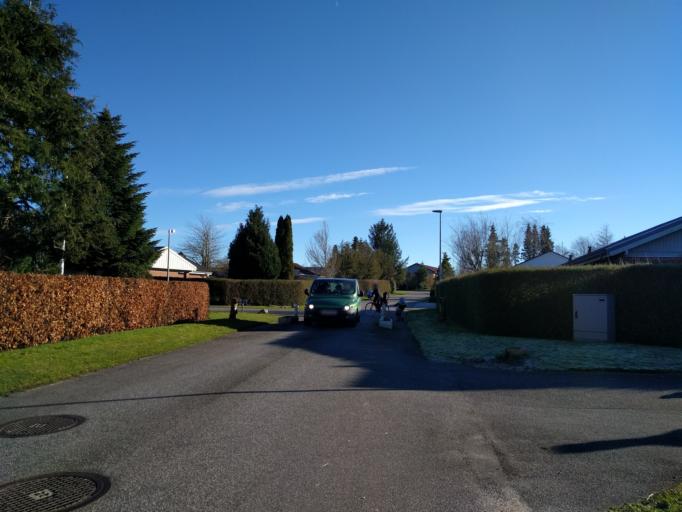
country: DK
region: Central Jutland
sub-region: Silkeborg Kommune
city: Silkeborg
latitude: 56.1853
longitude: 9.5164
